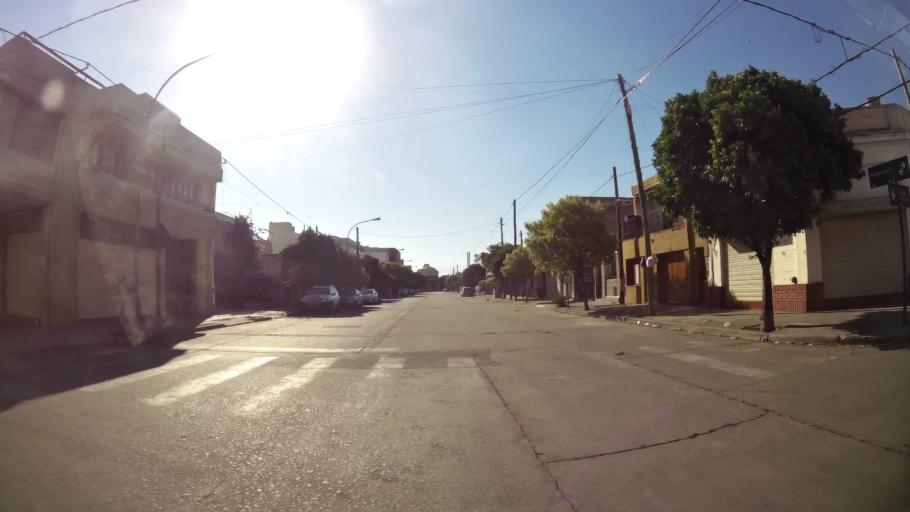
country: AR
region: Cordoba
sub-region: Departamento de Capital
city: Cordoba
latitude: -31.3934
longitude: -64.1735
